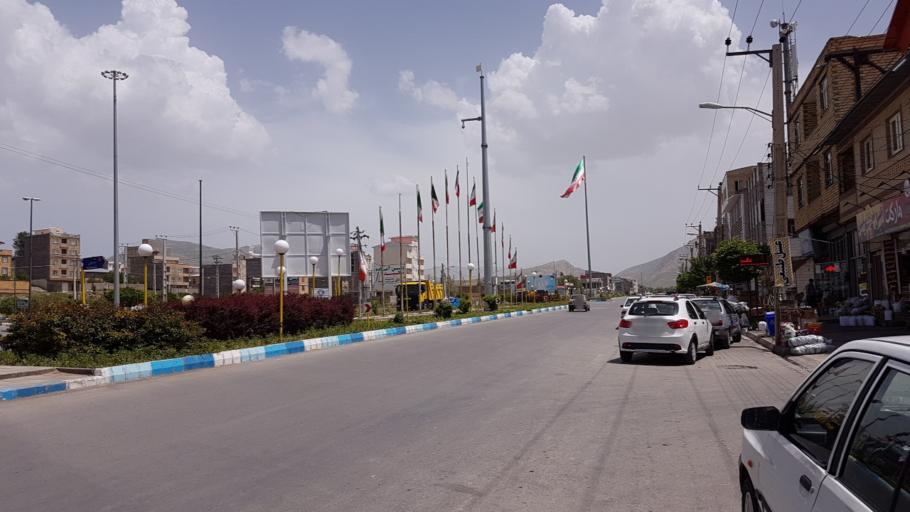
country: IR
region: Ardabil
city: Khalkhal
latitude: 37.6070
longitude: 48.5389
